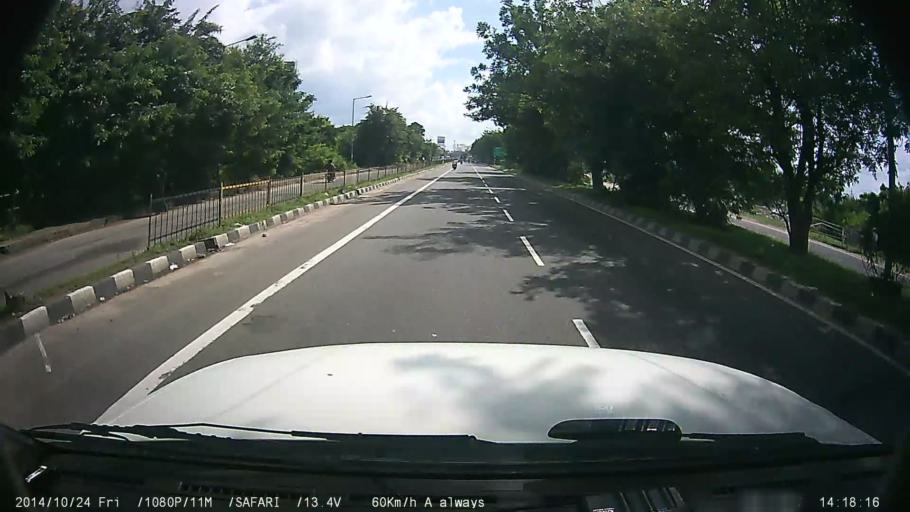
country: IN
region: Tamil Nadu
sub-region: Kancheepuram
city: Singapperumalkovil
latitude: 12.7670
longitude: 80.0057
